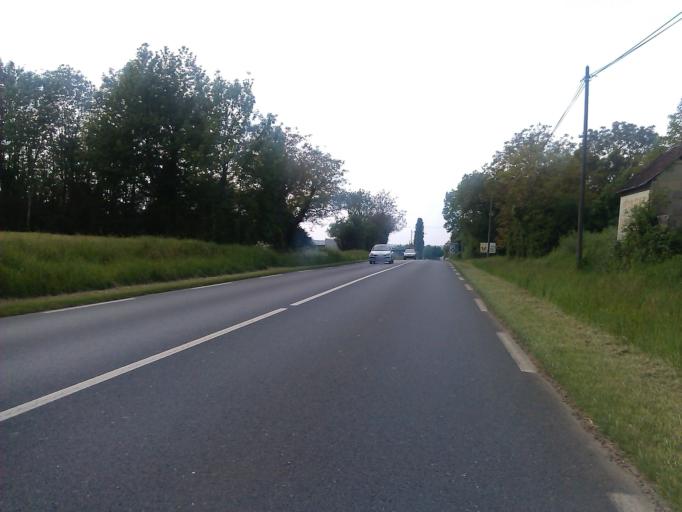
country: FR
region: Centre
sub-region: Departement de l'Indre
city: La Chatre
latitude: 46.5781
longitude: 2.0095
